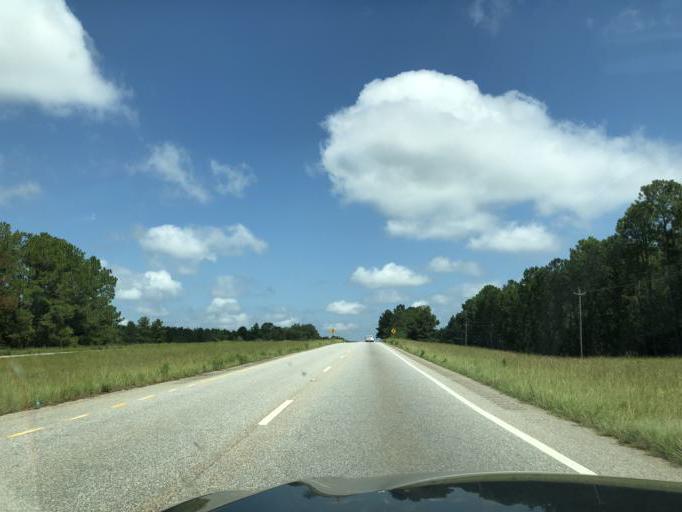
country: US
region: Alabama
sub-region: Henry County
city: Abbeville
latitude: 31.5748
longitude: -85.2804
